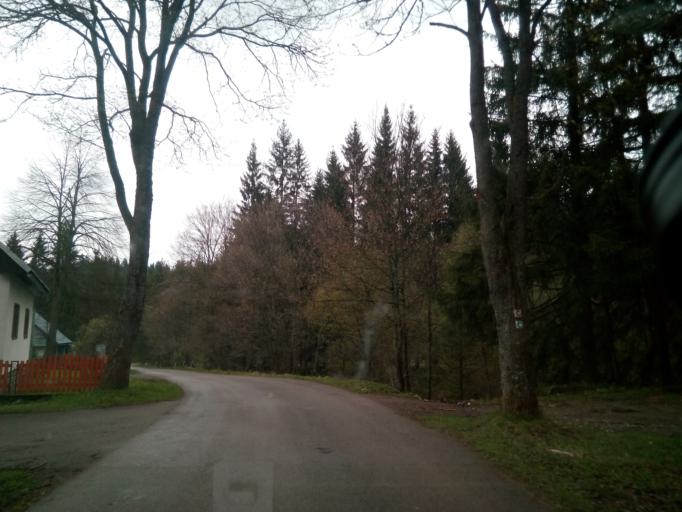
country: SK
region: Zilinsky
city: Oravska Lesna
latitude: 49.3577
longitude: 19.1723
